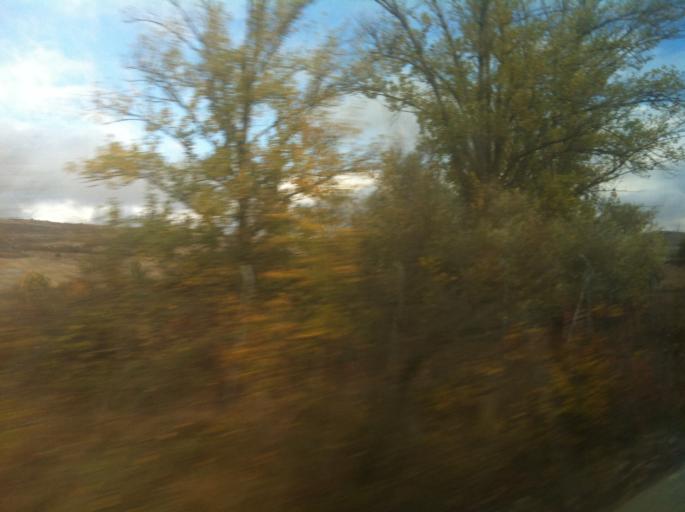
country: ES
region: Castille and Leon
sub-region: Provincia de Burgos
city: Rubena
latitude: 42.3853
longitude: -3.5840
